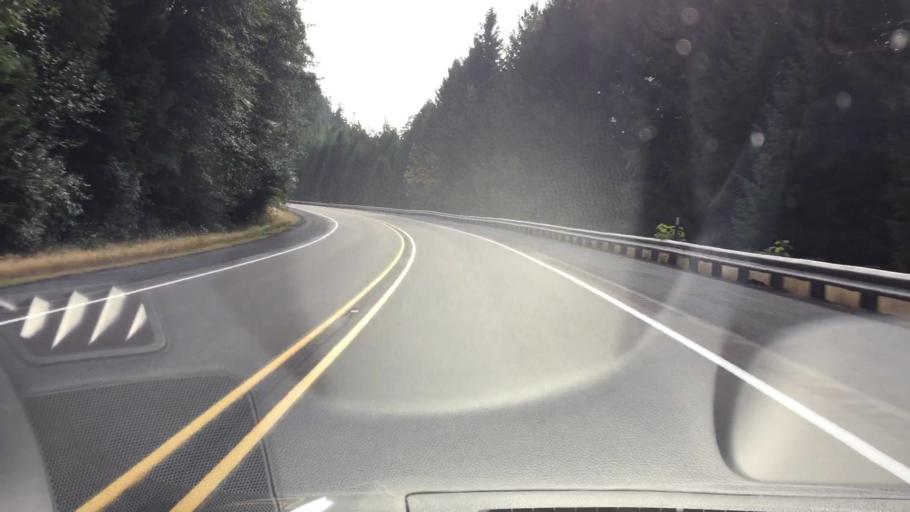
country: US
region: Washington
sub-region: Pierce County
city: Buckley
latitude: 46.6730
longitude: -121.5819
